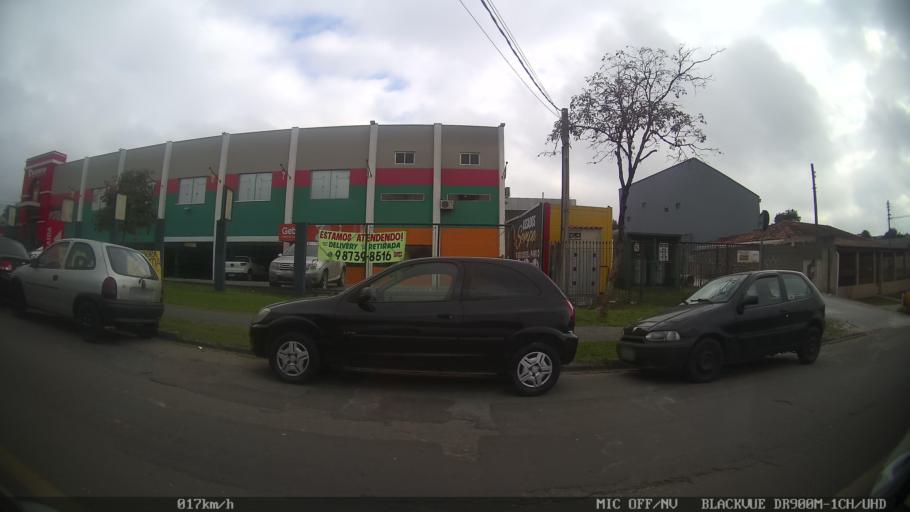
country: BR
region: Parana
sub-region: Curitiba
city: Curitiba
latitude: -25.3692
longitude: -49.2684
